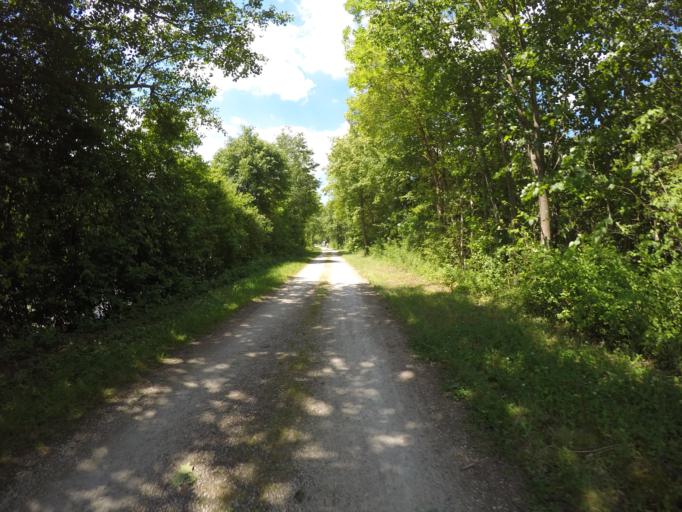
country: DE
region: Bavaria
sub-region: Lower Bavaria
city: Essing
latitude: 48.9350
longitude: 11.7875
